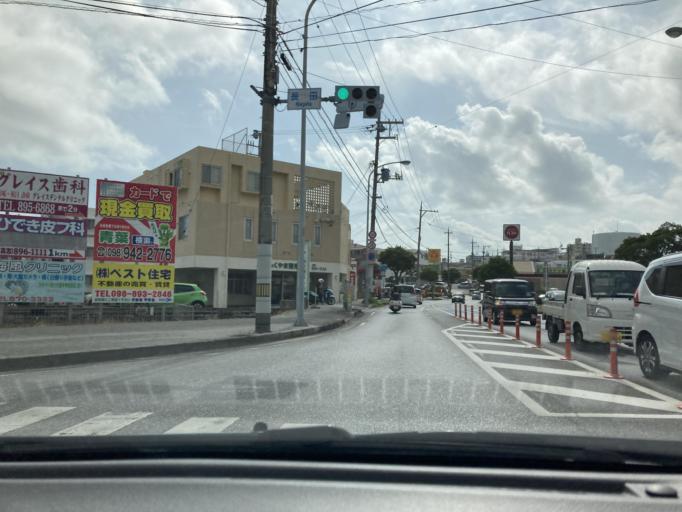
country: JP
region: Okinawa
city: Ginowan
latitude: 26.2627
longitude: 127.7616
